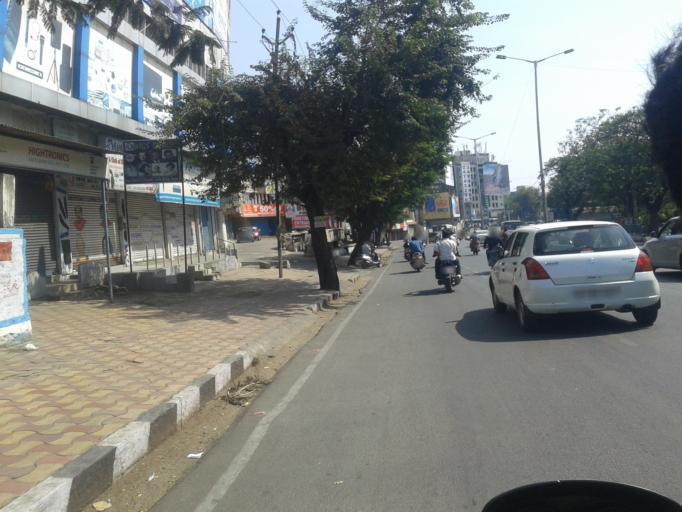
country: IN
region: Telangana
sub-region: Hyderabad
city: Hyderabad
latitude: 17.4083
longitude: 78.4762
